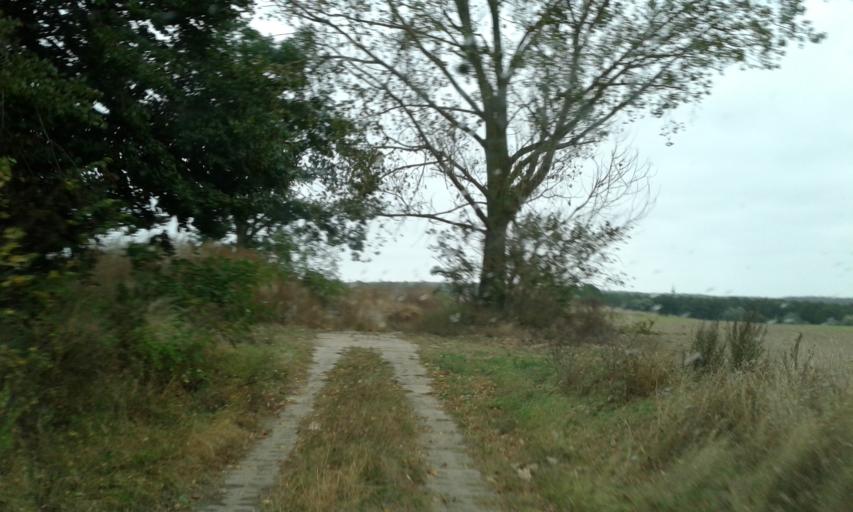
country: PL
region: West Pomeranian Voivodeship
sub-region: Powiat stargardzki
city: Dolice
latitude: 53.1089
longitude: 15.2229
